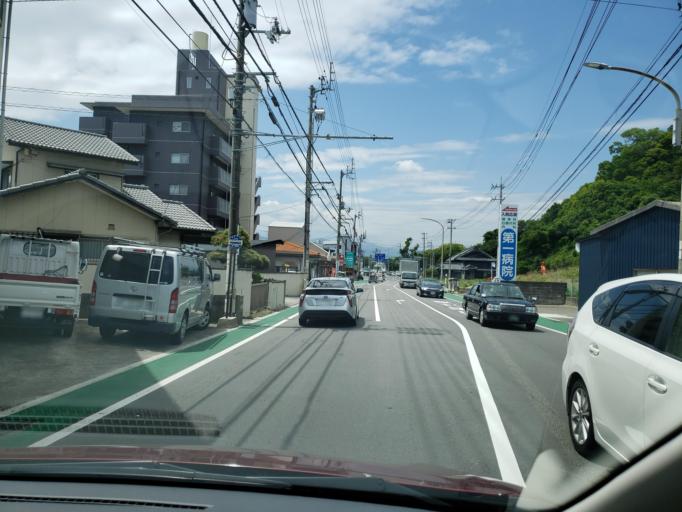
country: JP
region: Tokushima
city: Tokushima-shi
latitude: 34.0462
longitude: 134.5730
